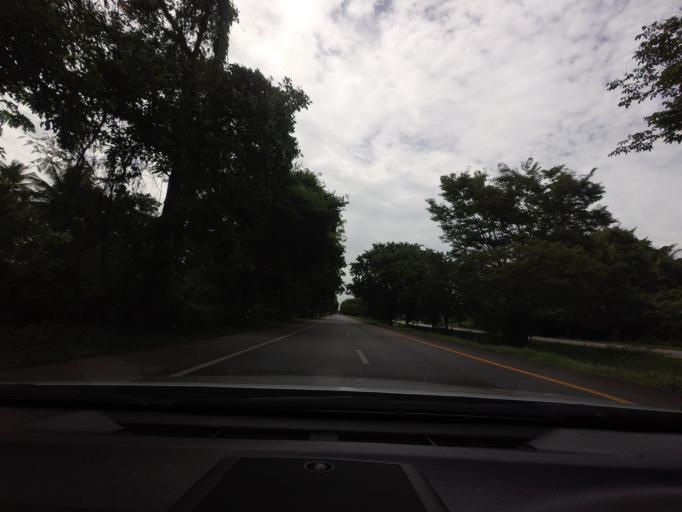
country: TH
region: Chumphon
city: Lamae
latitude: 9.7201
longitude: 99.1039
